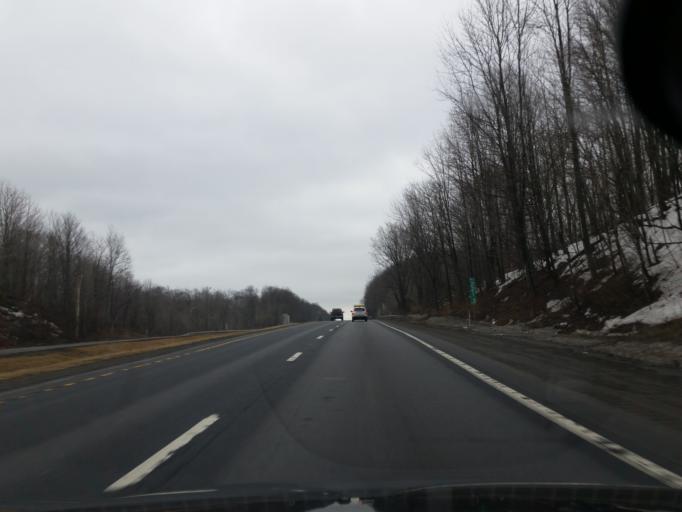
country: US
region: Pennsylvania
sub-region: Susquehanna County
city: Hallstead
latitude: 41.8521
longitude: -75.6840
